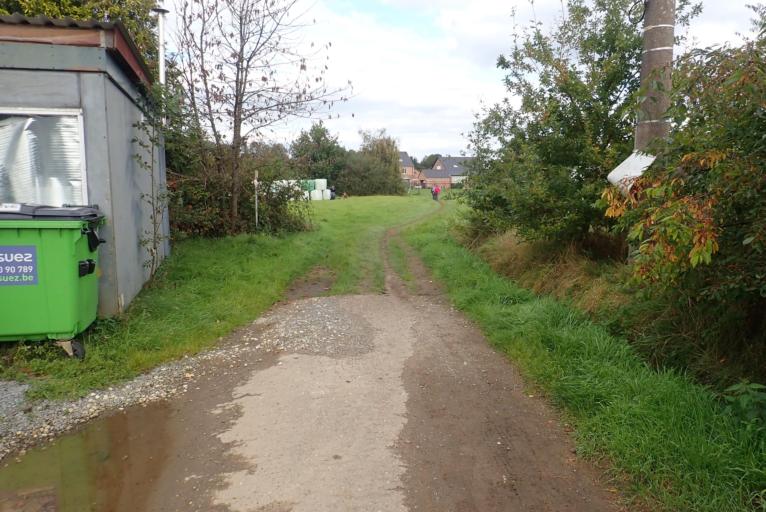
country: BE
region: Flanders
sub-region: Provincie Vlaams-Brabant
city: Aarschot
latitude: 50.9816
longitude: 4.8989
